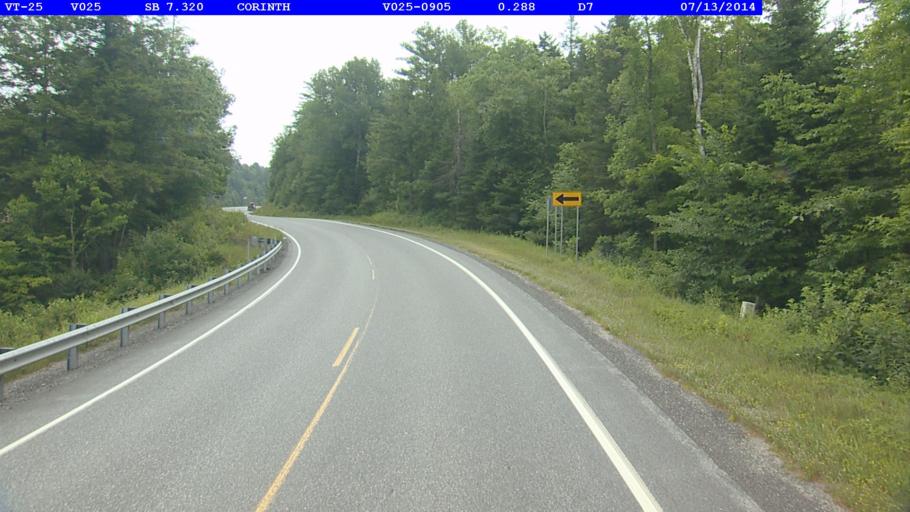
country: US
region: New Hampshire
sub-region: Grafton County
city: Haverhill
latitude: 44.0441
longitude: -72.2080
